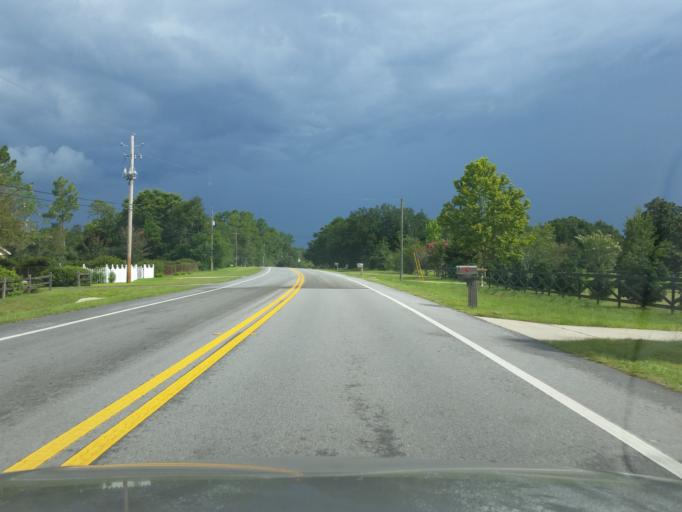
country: US
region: Florida
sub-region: Escambia County
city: Gonzalez
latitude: 30.5386
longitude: -87.3260
